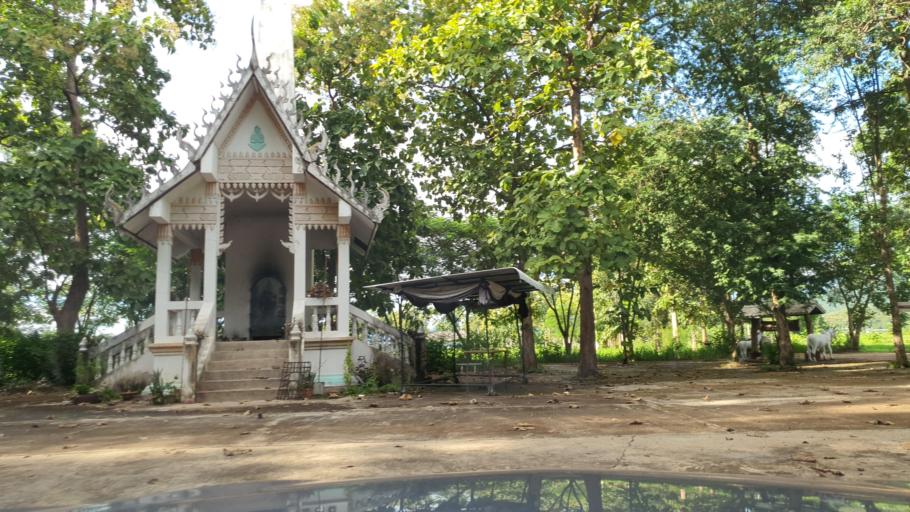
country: TH
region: Chiang Mai
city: Mae On
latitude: 18.7622
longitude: 99.2550
